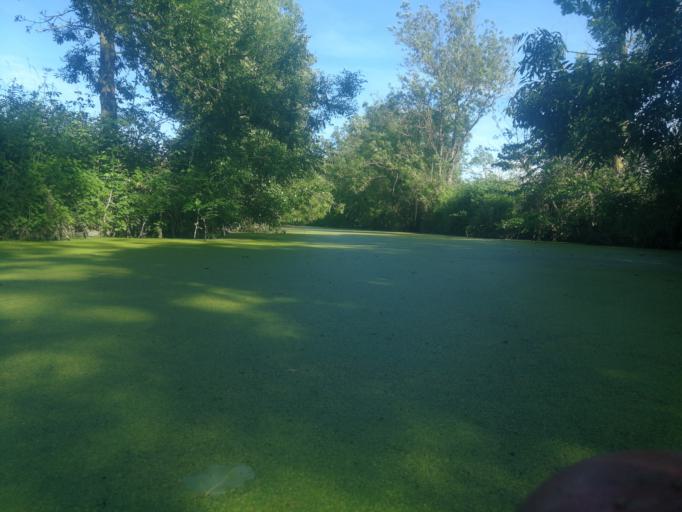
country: FR
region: Poitou-Charentes
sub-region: Departement de la Charente-Maritime
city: Marans
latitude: 46.3613
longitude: -0.9549
